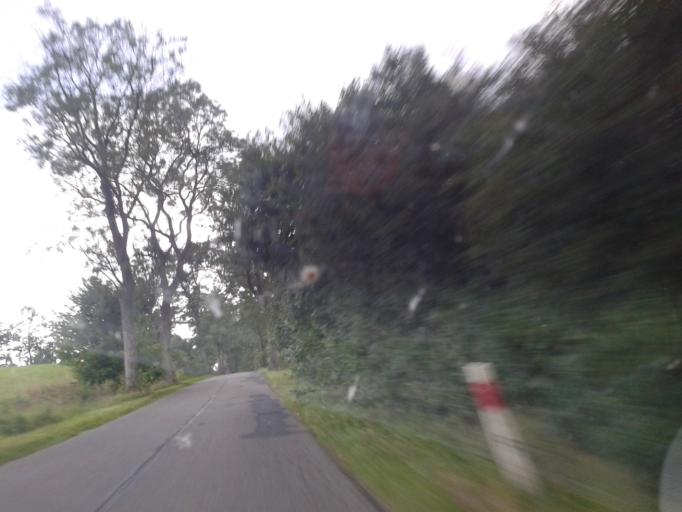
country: PL
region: West Pomeranian Voivodeship
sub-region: Powiat koszalinski
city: Bobolice
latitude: 53.9003
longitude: 16.5319
